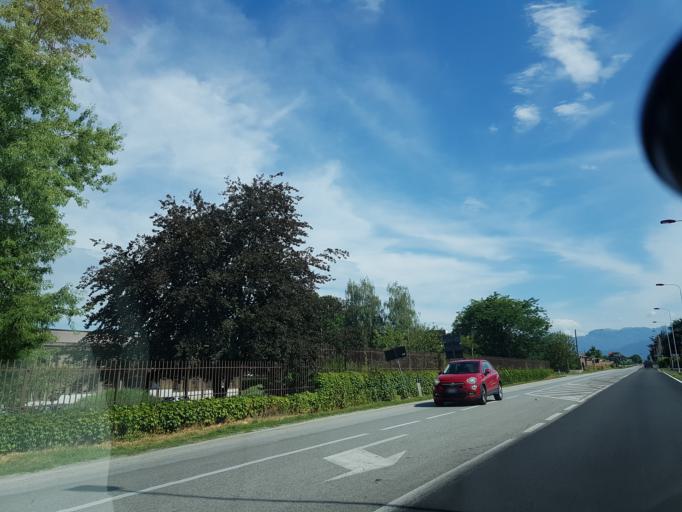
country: IT
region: Piedmont
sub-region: Provincia di Cuneo
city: Roata Rossi
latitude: 44.4243
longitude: 7.5432
